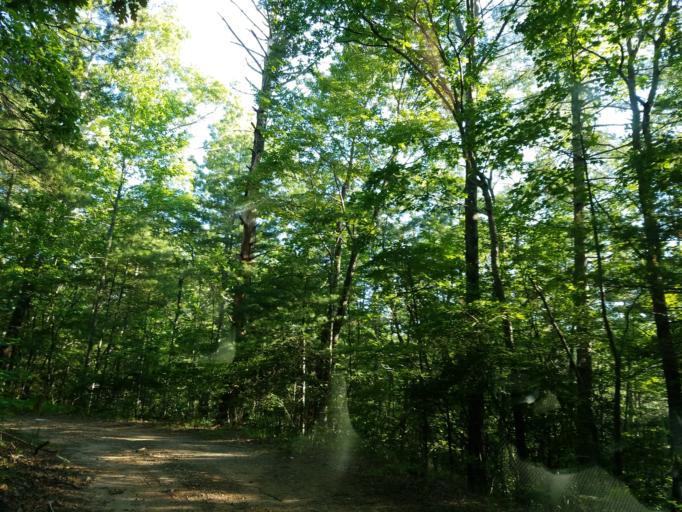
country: US
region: Georgia
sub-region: Fannin County
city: Blue Ridge
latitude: 34.8033
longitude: -84.1749
